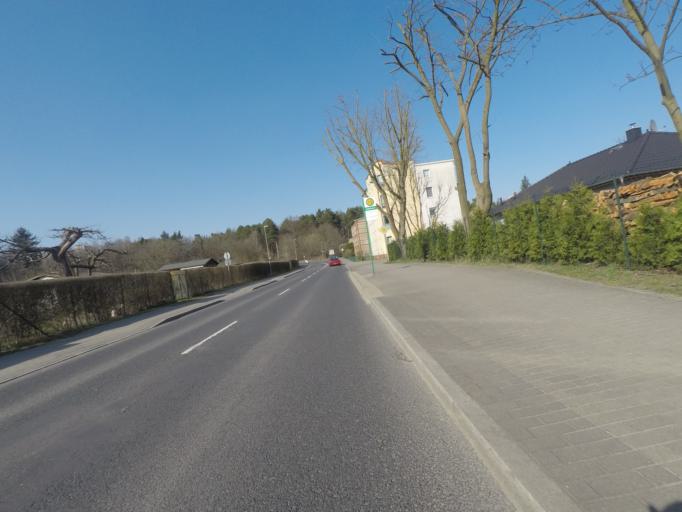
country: DE
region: Brandenburg
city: Eberswalde
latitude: 52.8429
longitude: 13.7907
